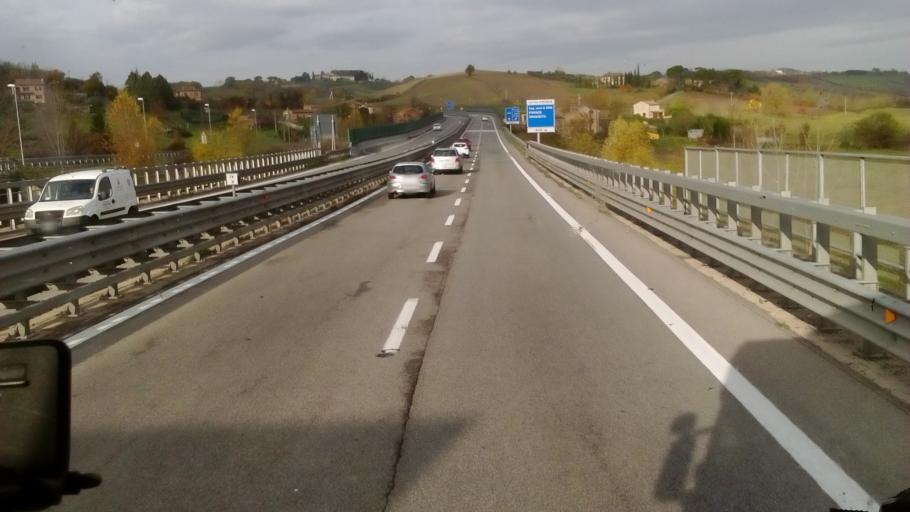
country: IT
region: Tuscany
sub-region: Provincia di Siena
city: Taverne D'Arbia
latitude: 43.2989
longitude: 11.3870
